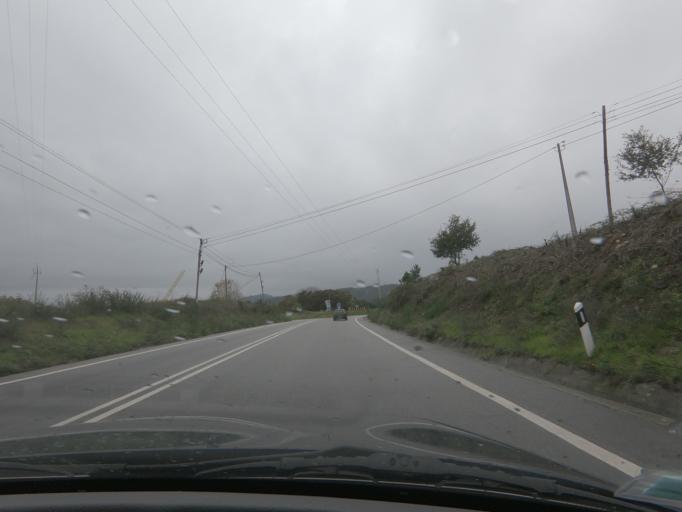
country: PT
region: Porto
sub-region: Amarante
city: Teloes
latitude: 41.3002
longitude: -8.0855
